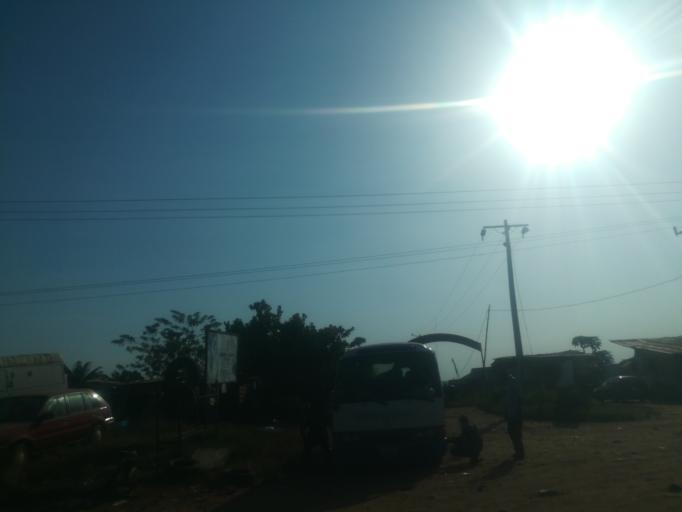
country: NG
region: Ogun
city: Abeokuta
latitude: 7.1778
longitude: 3.2861
